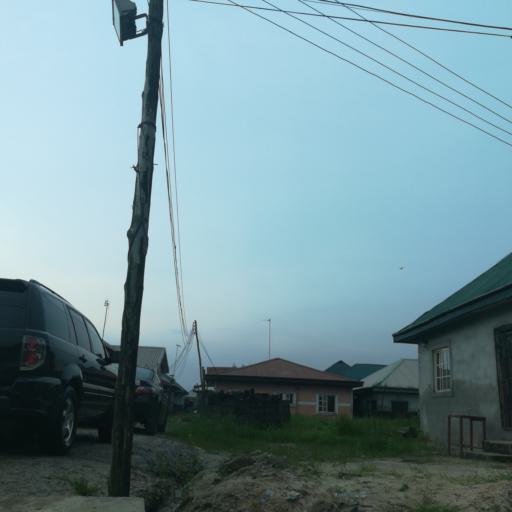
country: NG
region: Rivers
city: Port Harcourt
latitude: 4.7466
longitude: 7.0070
